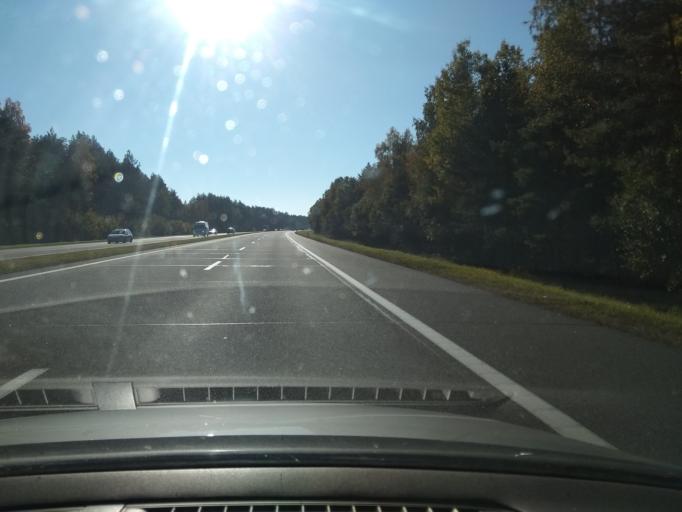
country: BY
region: Brest
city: Baranovichi
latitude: 53.0593
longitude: 25.8660
